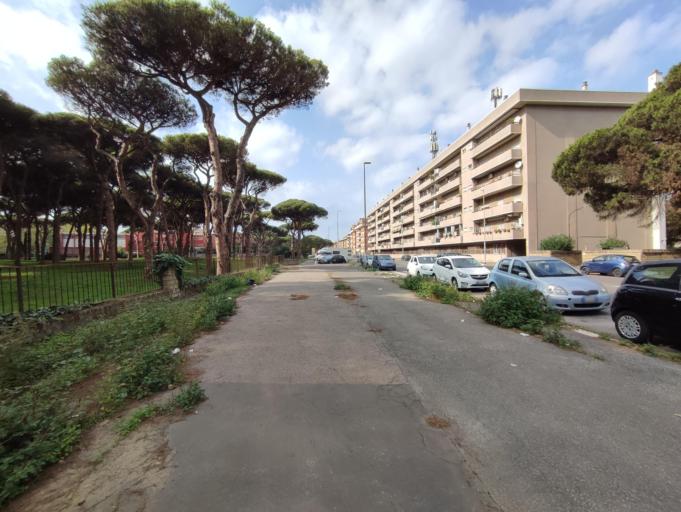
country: IT
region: Latium
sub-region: Citta metropolitana di Roma Capitale
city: Lido di Ostia
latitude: 41.7339
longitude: 12.2977
